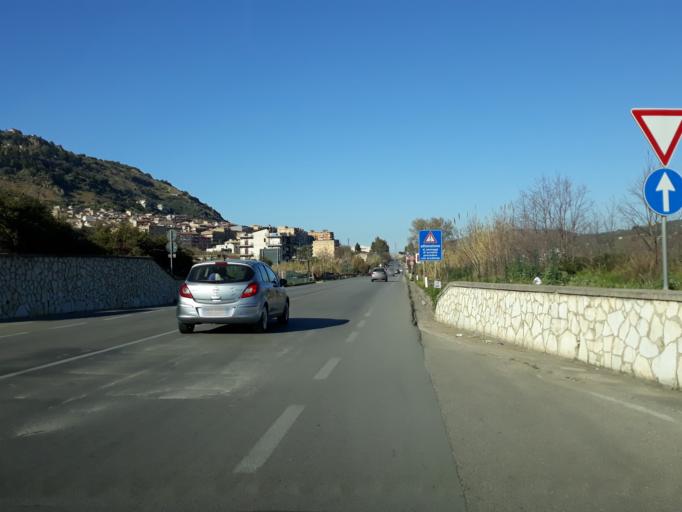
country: IT
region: Sicily
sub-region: Palermo
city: Misilmeri
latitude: 38.0289
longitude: 13.4558
